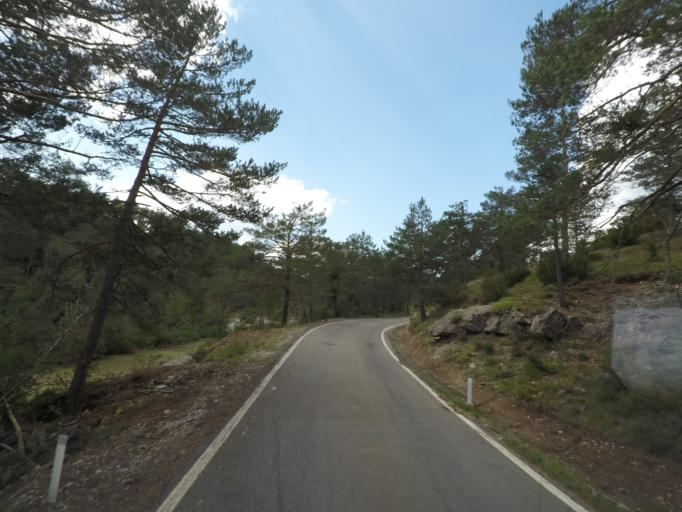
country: ES
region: Aragon
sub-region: Provincia de Huesca
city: Fiscal
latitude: 42.4059
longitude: -0.1745
